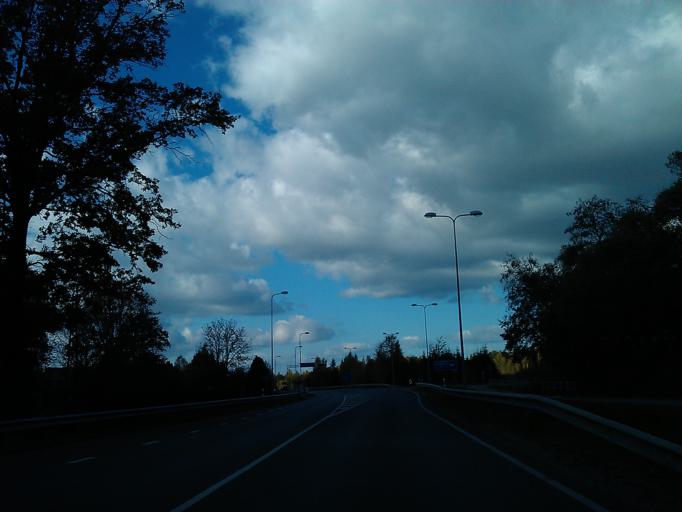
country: LV
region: Livani
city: Livani
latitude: 56.3884
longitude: 26.1530
